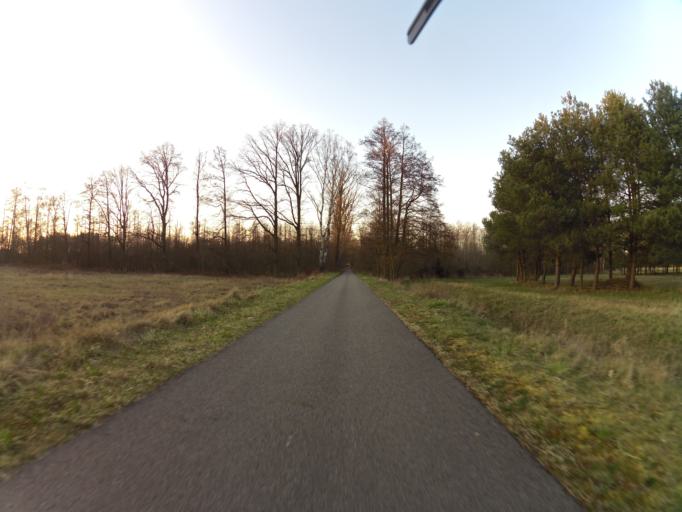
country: PL
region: West Pomeranian Voivodeship
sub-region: Powiat policki
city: Nowe Warpno
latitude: 53.7063
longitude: 14.3153
